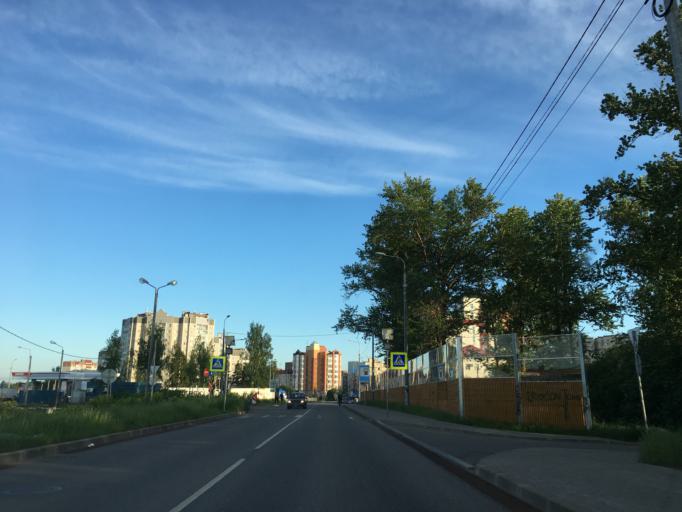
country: RU
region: Leningrad
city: Gatchina
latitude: 59.5822
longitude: 30.1370
